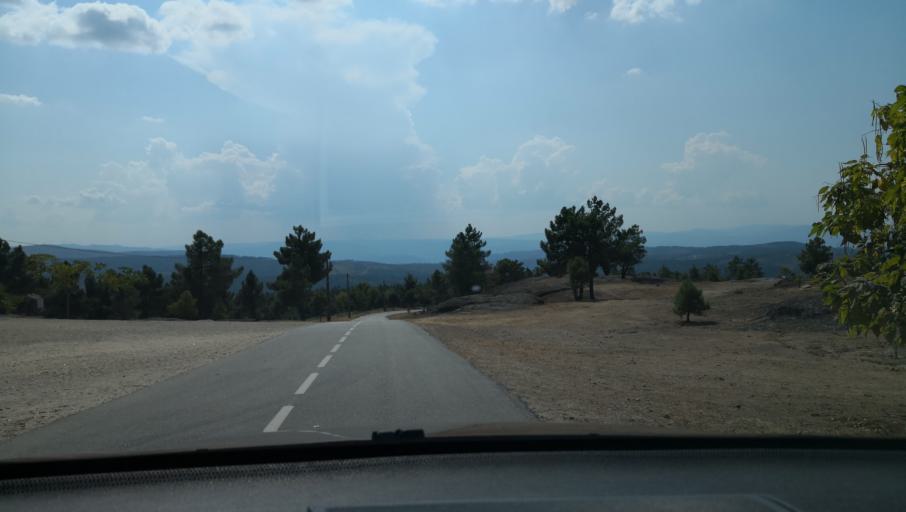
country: PT
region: Vila Real
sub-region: Sabrosa
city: Sabrosa
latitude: 41.2784
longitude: -7.6179
